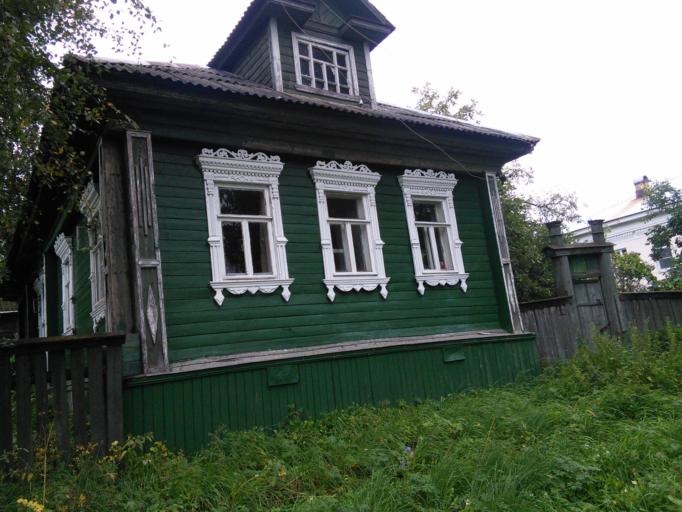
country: RU
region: Jaroslavl
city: Tutayev
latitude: 57.8803
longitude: 39.5377
